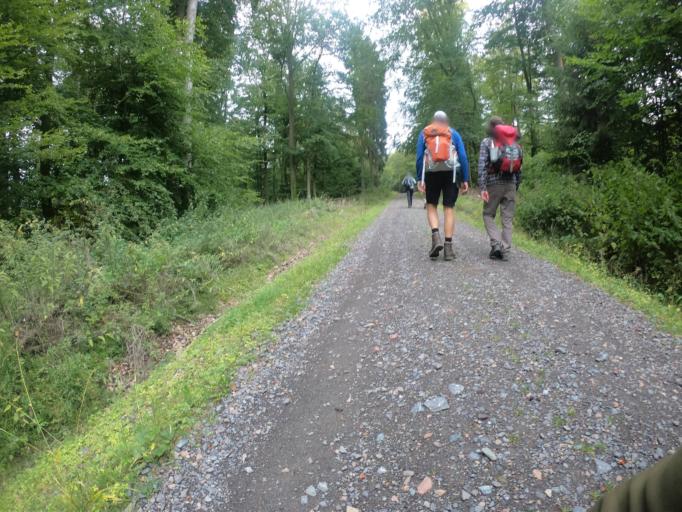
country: DE
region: Hesse
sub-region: Regierungsbezirk Darmstadt
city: Waldems
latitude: 50.2106
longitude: 8.3160
